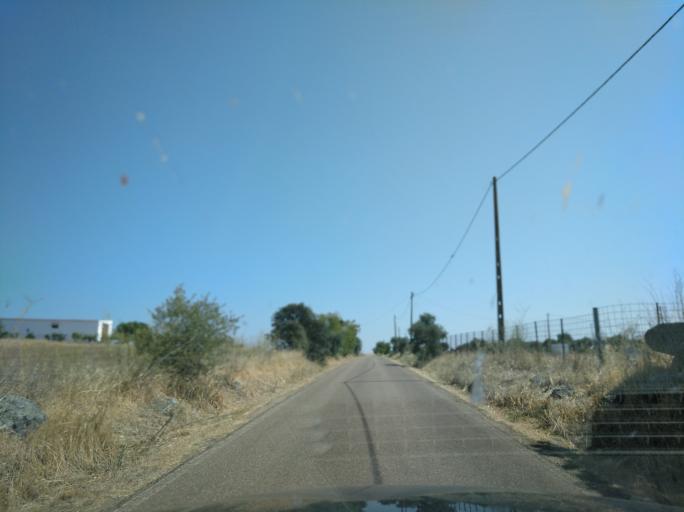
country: PT
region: Portalegre
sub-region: Campo Maior
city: Campo Maior
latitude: 39.0223
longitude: -7.0487
